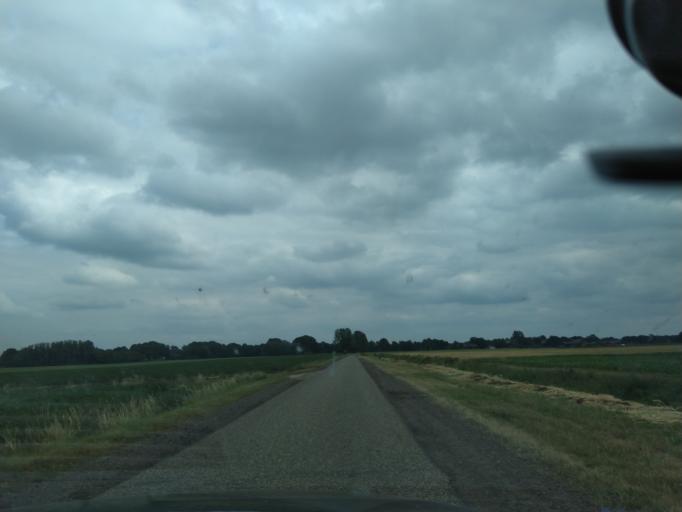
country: NL
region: Groningen
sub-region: Gemeente Vlagtwedde
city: Vlagtwedde
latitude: 53.0816
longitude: 7.1105
